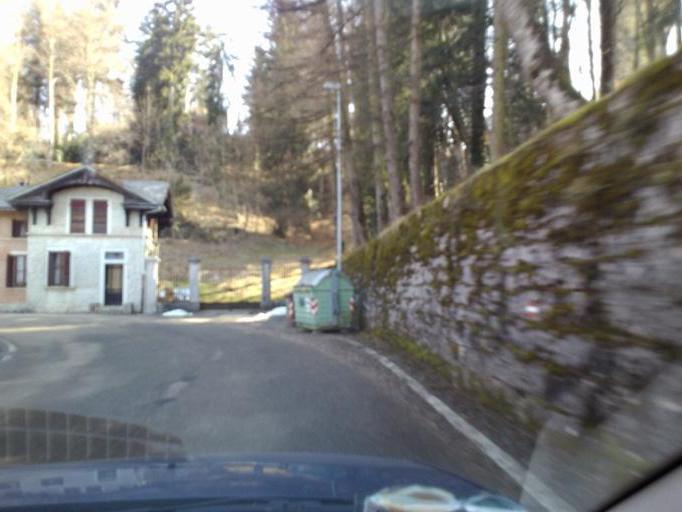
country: IT
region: Veneto
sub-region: Provincia di Verona
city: Bosco Chiesanuova
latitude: 45.6230
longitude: 11.0317
